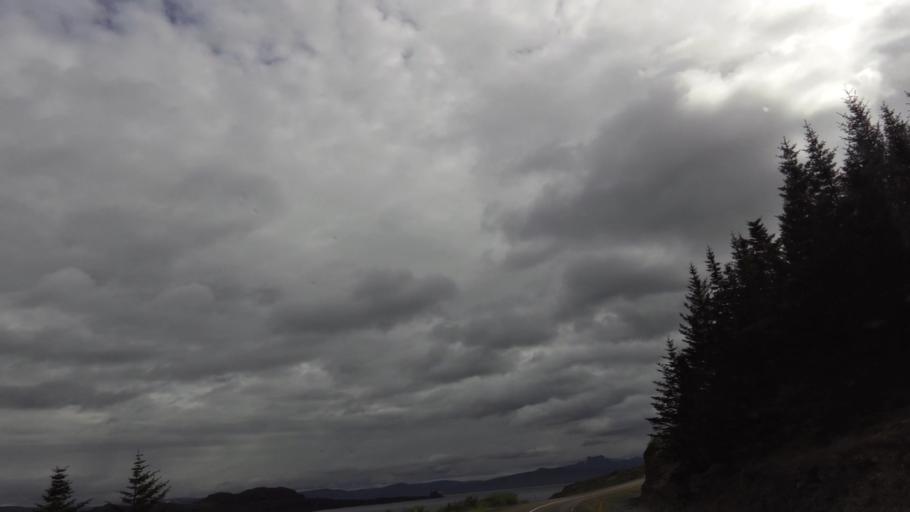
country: IS
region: West
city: Stykkisholmur
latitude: 65.5158
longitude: -22.1110
